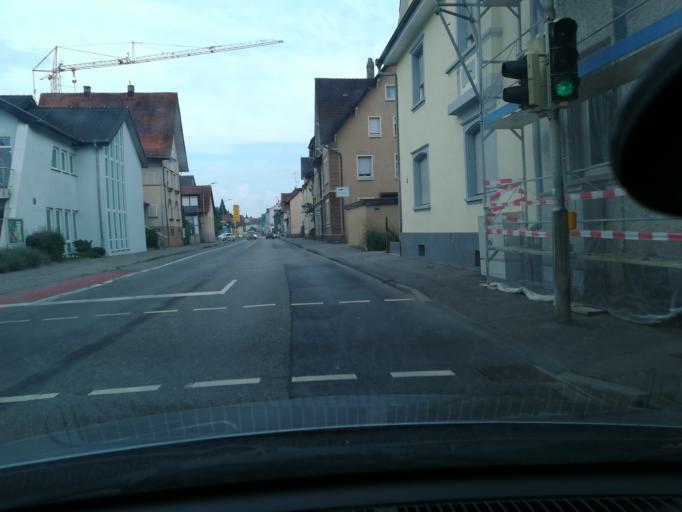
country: DE
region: Baden-Wuerttemberg
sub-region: Freiburg Region
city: Singen
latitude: 47.7657
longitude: 8.8296
